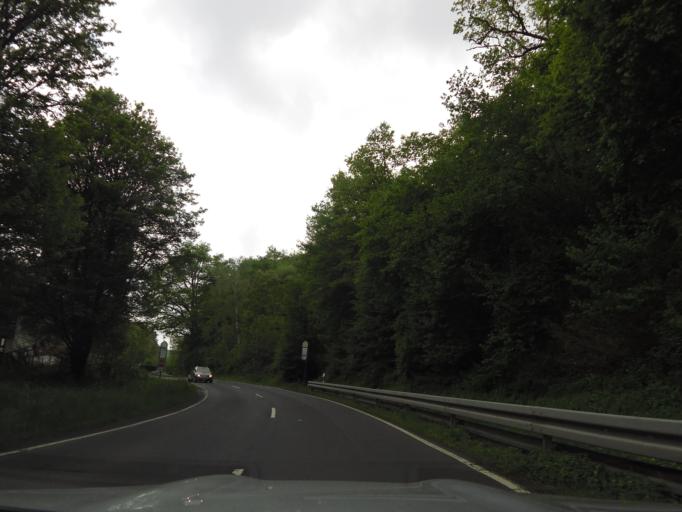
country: DE
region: Hesse
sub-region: Regierungsbezirk Giessen
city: Braunfels
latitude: 50.5229
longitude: 8.3799
